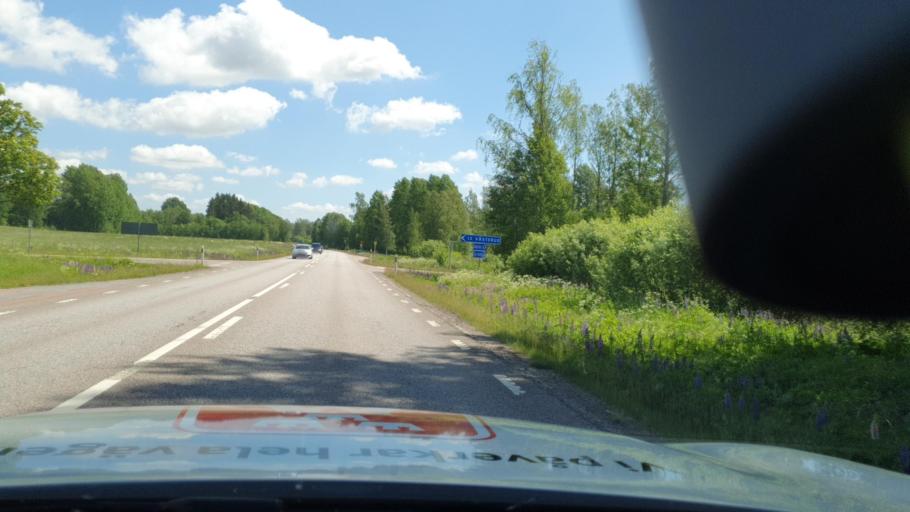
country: SE
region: Vaermland
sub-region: Karlstads Kommun
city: Molkom
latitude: 59.6097
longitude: 13.8110
